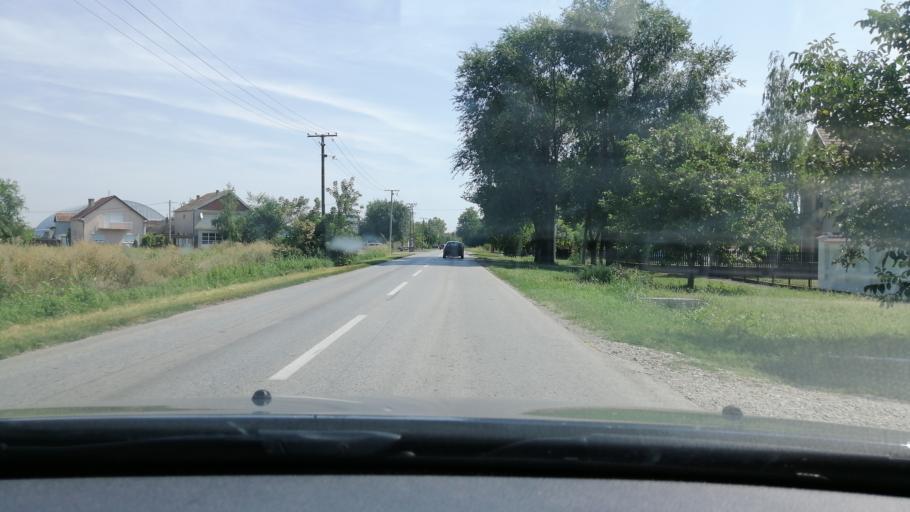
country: RS
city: Lazarevo
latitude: 45.3878
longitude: 20.5244
